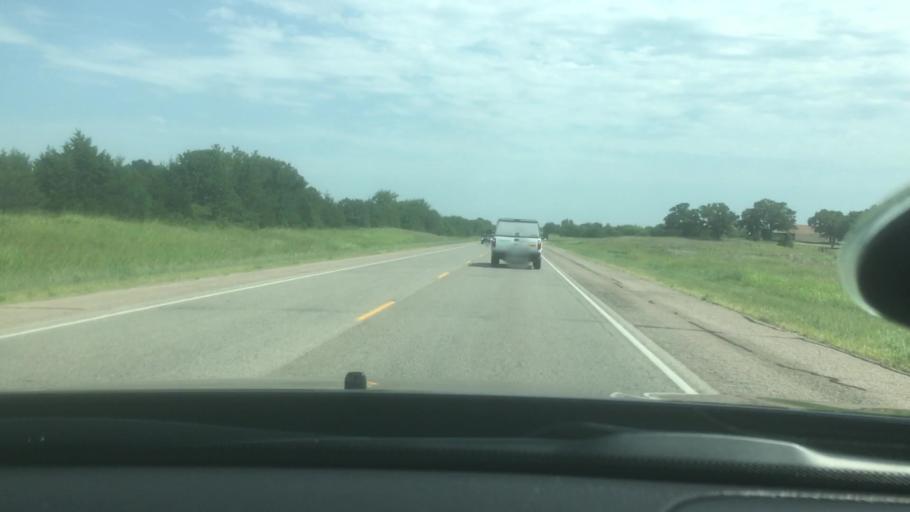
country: US
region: Oklahoma
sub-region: Seminole County
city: Maud
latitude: 35.0342
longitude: -96.9314
